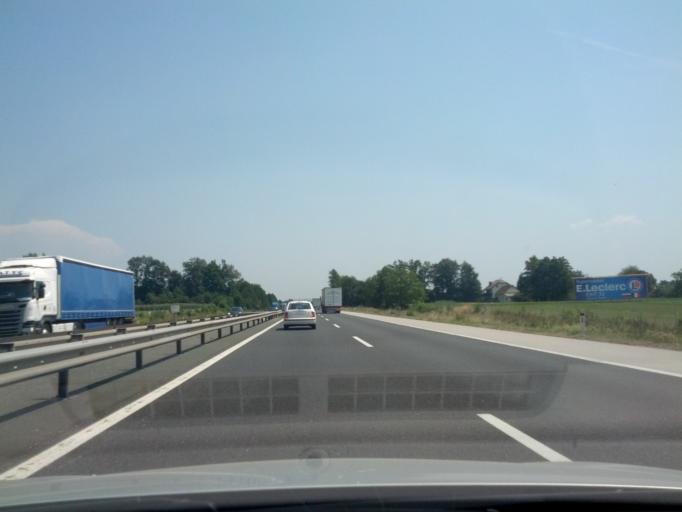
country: SI
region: Brezovica
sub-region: Opstina Ljubljana-Vic-Rudnik
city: Brezovica pri Ljubljani
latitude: 46.0195
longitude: 14.4007
